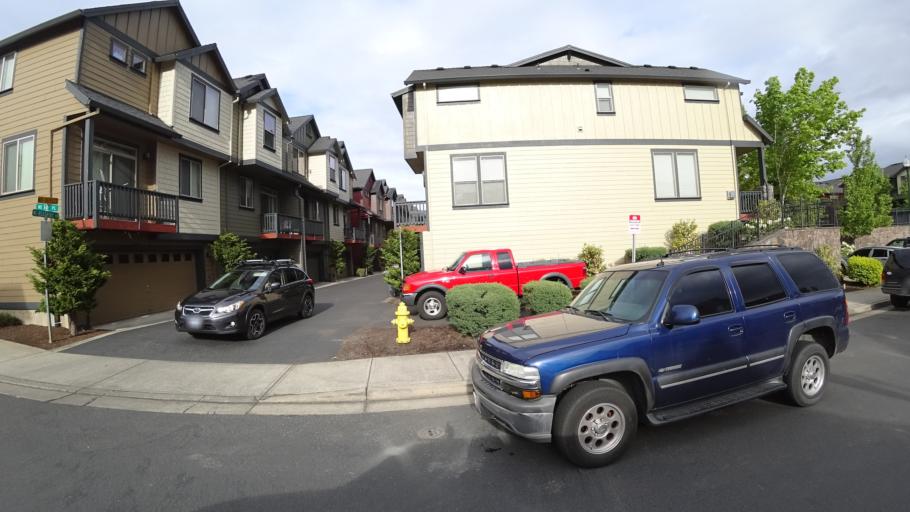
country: US
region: Oregon
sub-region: Washington County
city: Hillsboro
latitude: 45.5483
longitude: -122.9680
